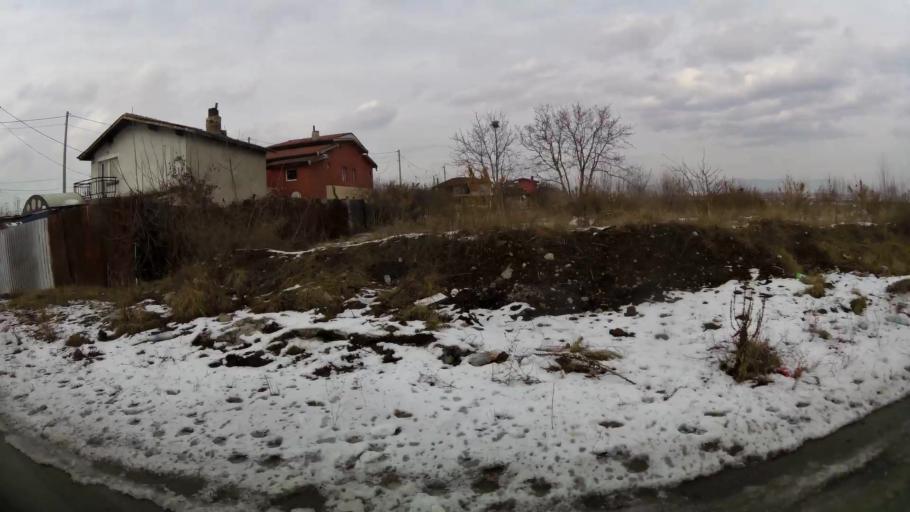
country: BG
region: Sofia-Capital
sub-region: Stolichna Obshtina
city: Sofia
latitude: 42.6915
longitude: 23.3880
